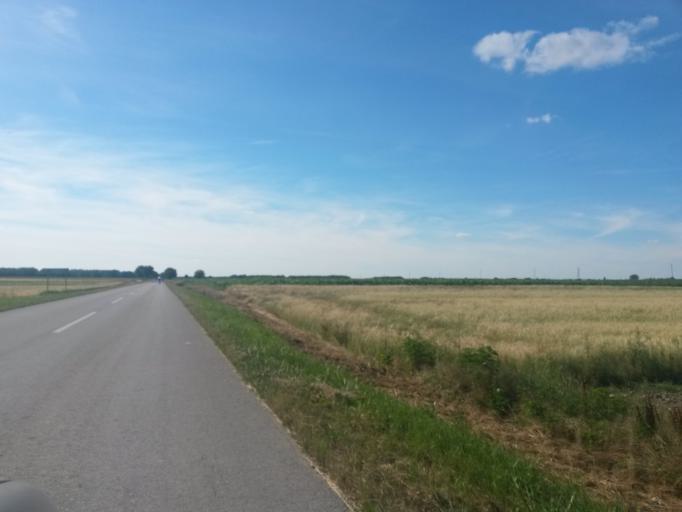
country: HR
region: Osjecko-Baranjska
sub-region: Grad Osijek
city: Bilje
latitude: 45.6003
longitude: 18.7777
